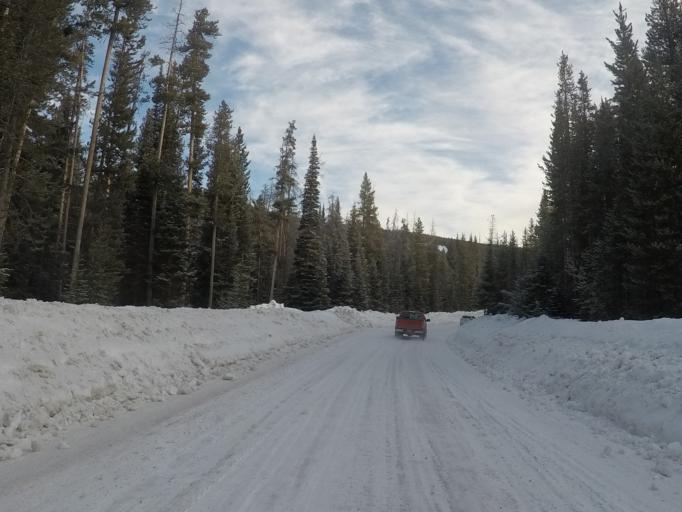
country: US
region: Montana
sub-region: Granite County
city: Philipsburg
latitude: 46.2445
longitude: -113.2440
